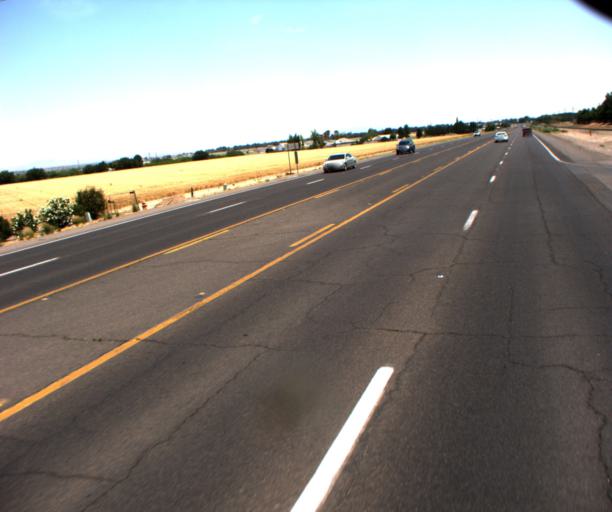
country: US
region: Arizona
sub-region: Graham County
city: Thatcher
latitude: 32.8635
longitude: -109.7889
